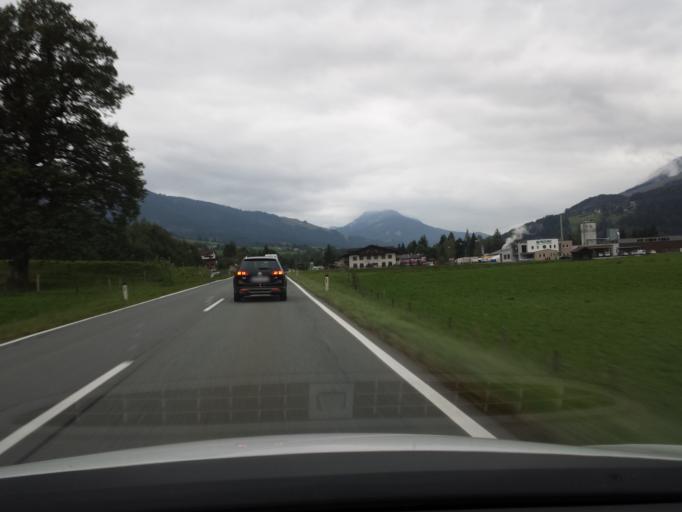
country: AT
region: Salzburg
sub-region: Politischer Bezirk Zell am See
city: Leogang
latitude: 47.4392
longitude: 12.7906
